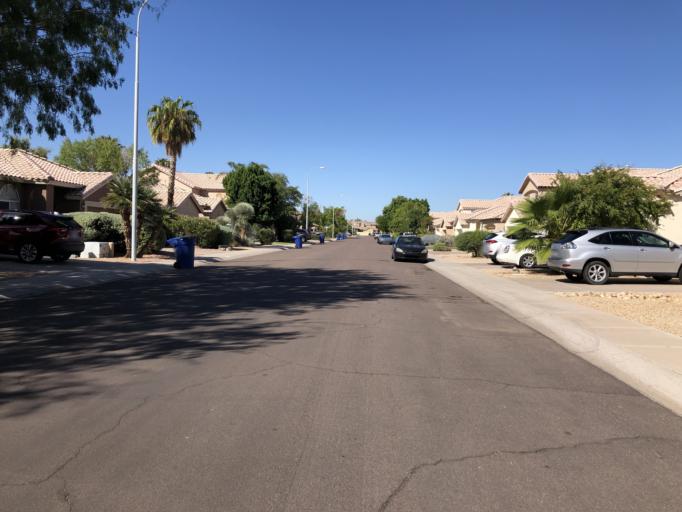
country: US
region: Arizona
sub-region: Maricopa County
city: Guadalupe
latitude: 33.3067
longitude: -111.9213
